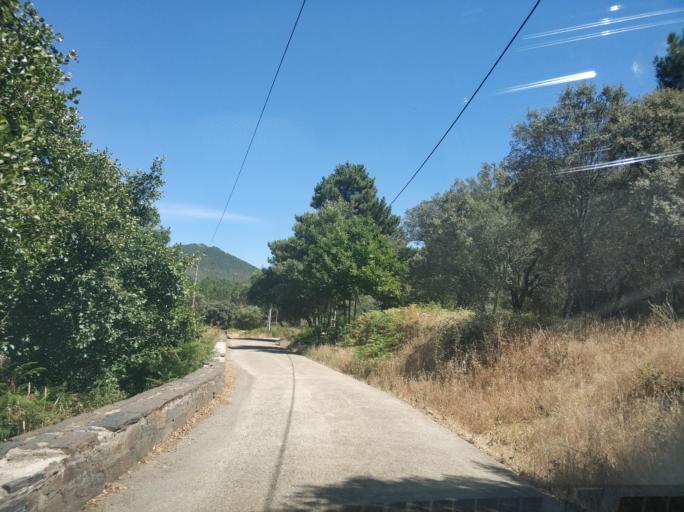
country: ES
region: Castille and Leon
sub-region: Provincia de Salamanca
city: Herguijuela de la Sierra
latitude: 40.4022
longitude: -6.0828
